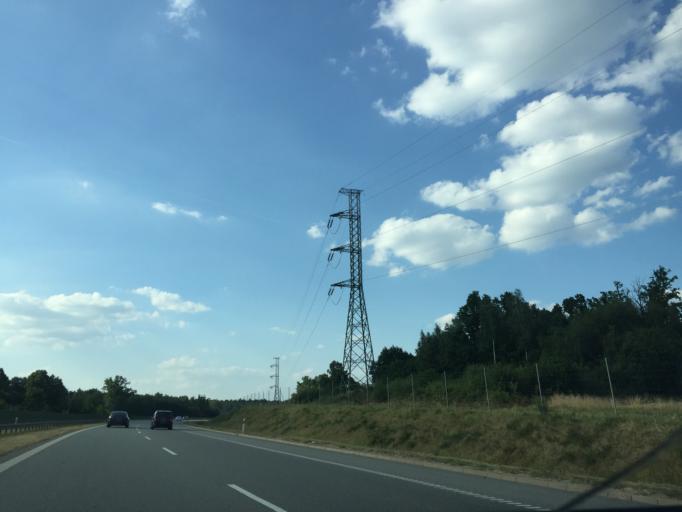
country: PL
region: Swietokrzyskie
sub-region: Powiat kielecki
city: Checiny
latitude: 50.8215
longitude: 20.4697
